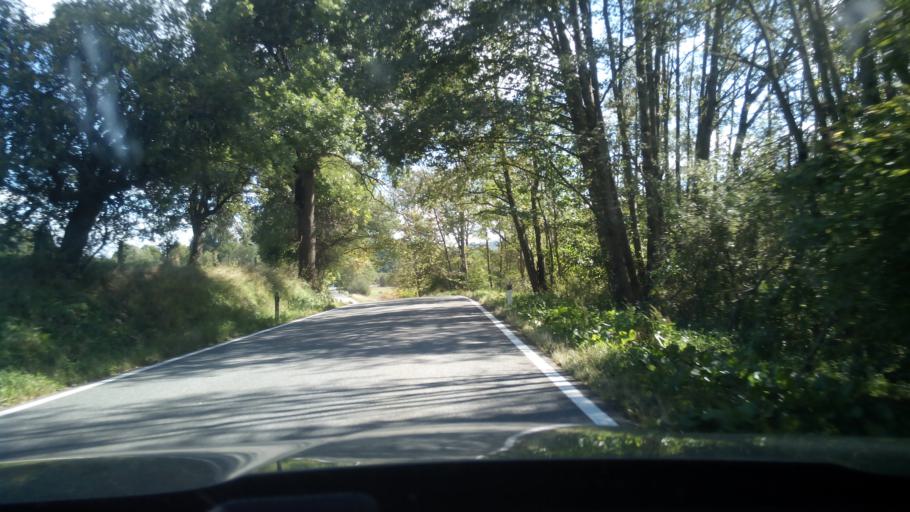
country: CZ
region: Jihocesky
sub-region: Okres Prachatice
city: Stachy
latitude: 49.1193
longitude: 13.6357
